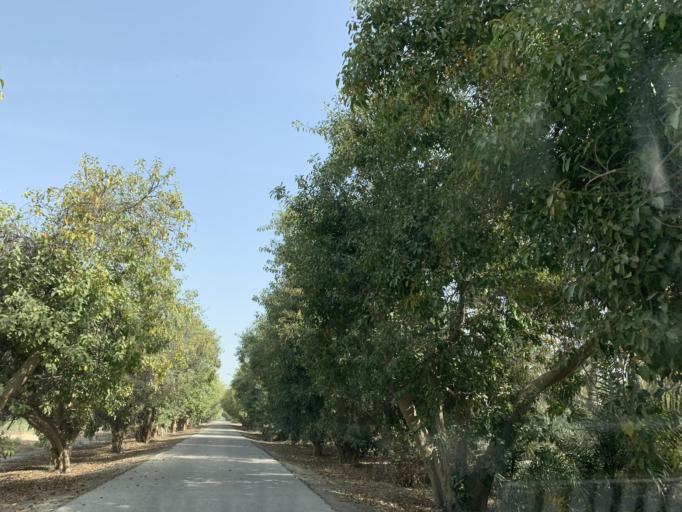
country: BH
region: Northern
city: Madinat `Isa
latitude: 26.1652
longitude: 50.5302
